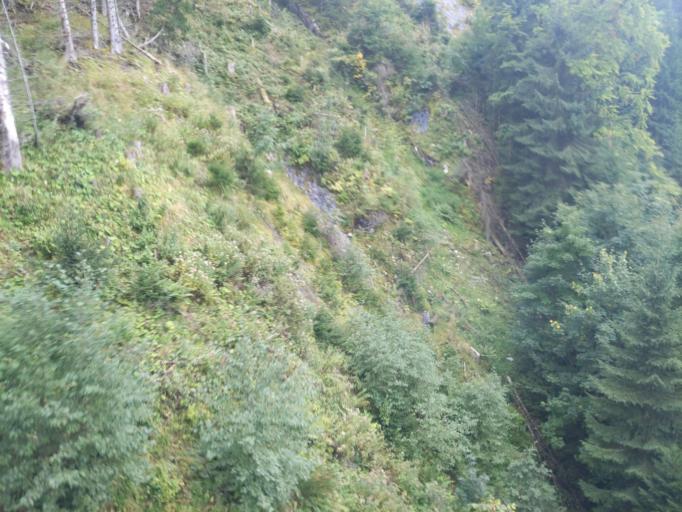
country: DE
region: Bavaria
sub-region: Upper Bavaria
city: Grainau
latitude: 47.4605
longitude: 11.0579
